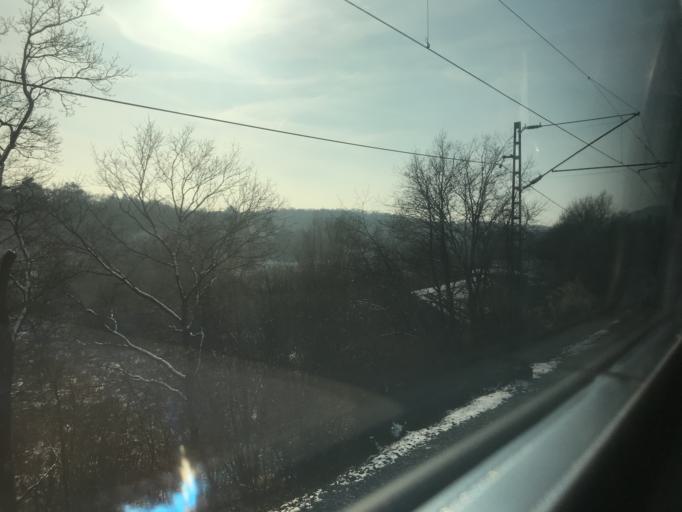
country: DE
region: Rheinland-Pfalz
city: Dreis
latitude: 49.9184
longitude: 6.8283
